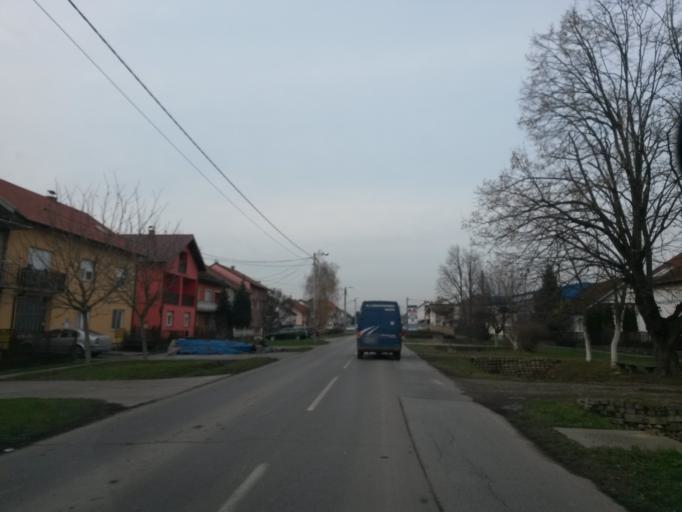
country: HR
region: Osjecko-Baranjska
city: Tenja
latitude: 45.5163
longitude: 18.7314
